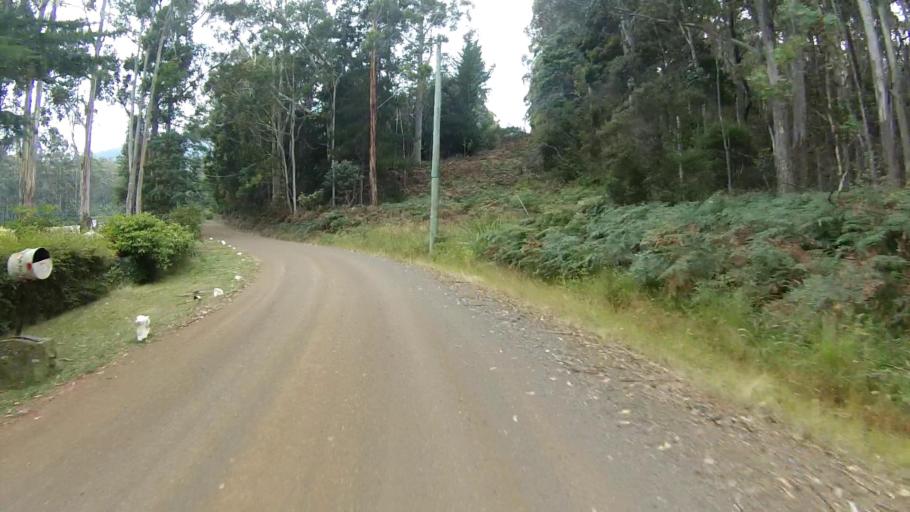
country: AU
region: Tasmania
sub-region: Huon Valley
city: Cygnet
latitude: -43.2328
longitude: 147.1587
